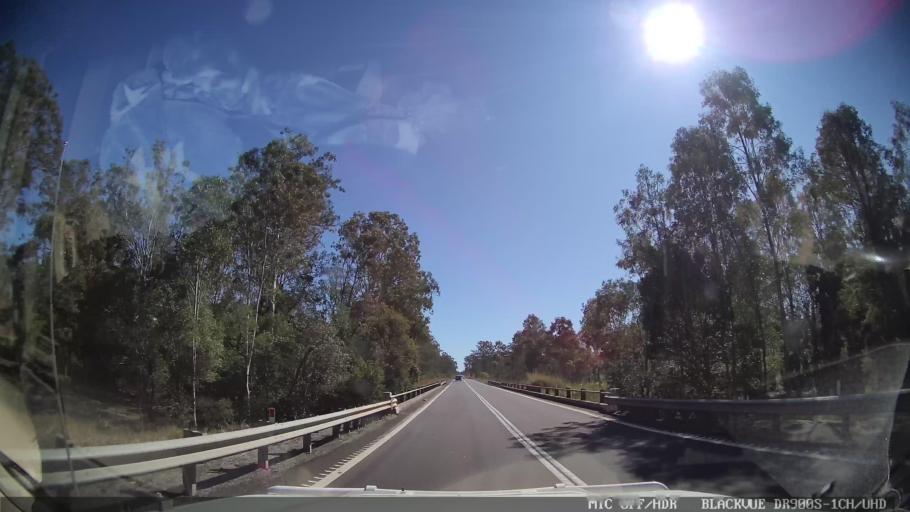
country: AU
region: Queensland
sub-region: Gympie Regional Council
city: Gympie
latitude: -26.0428
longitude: 152.5717
